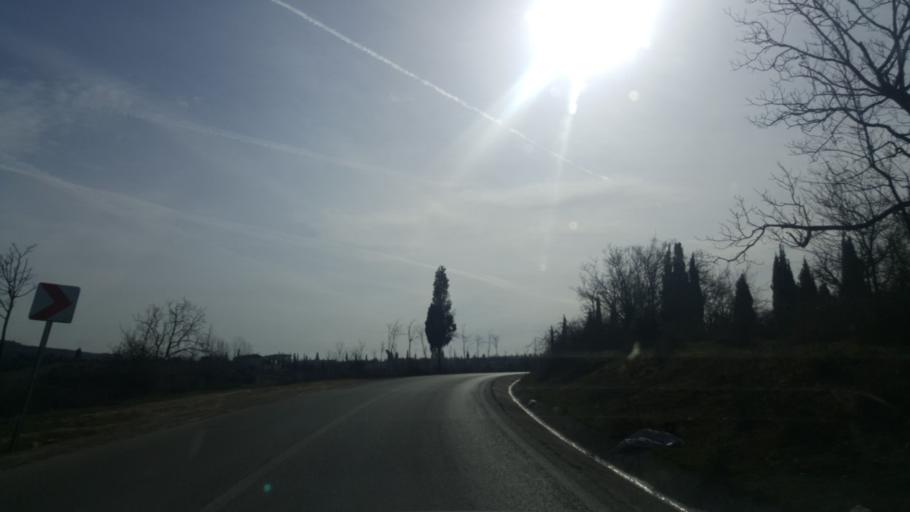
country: TR
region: Kocaeli
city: Tavsancil
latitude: 40.7887
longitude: 29.5705
